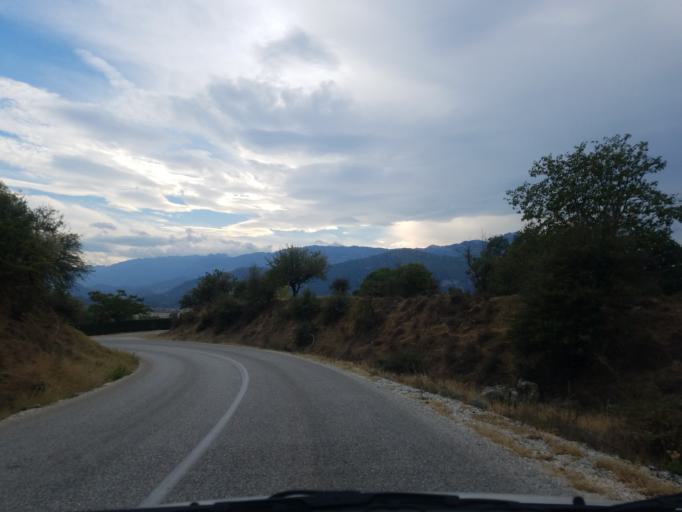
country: GR
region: Thessaly
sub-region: Trikala
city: Kalampaka
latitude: 39.7026
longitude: 21.6483
